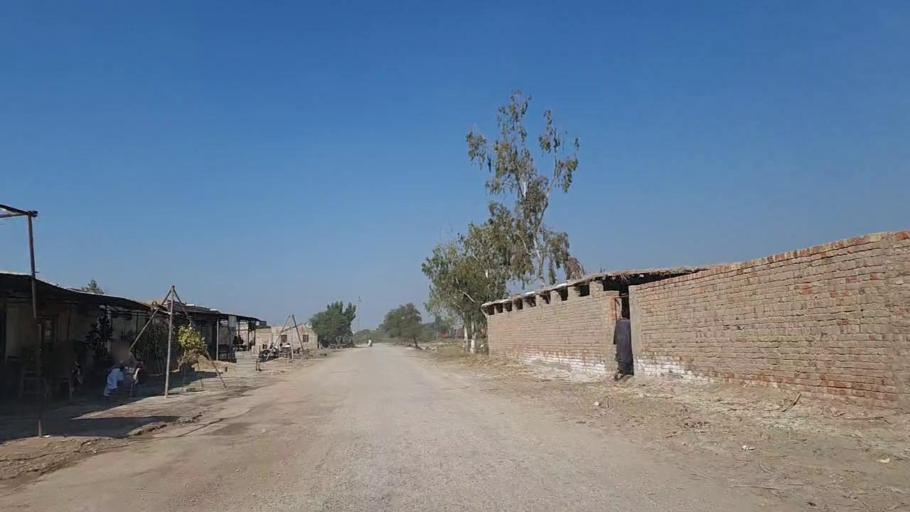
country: PK
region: Sindh
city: Nawabshah
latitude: 26.3483
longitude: 68.3675
